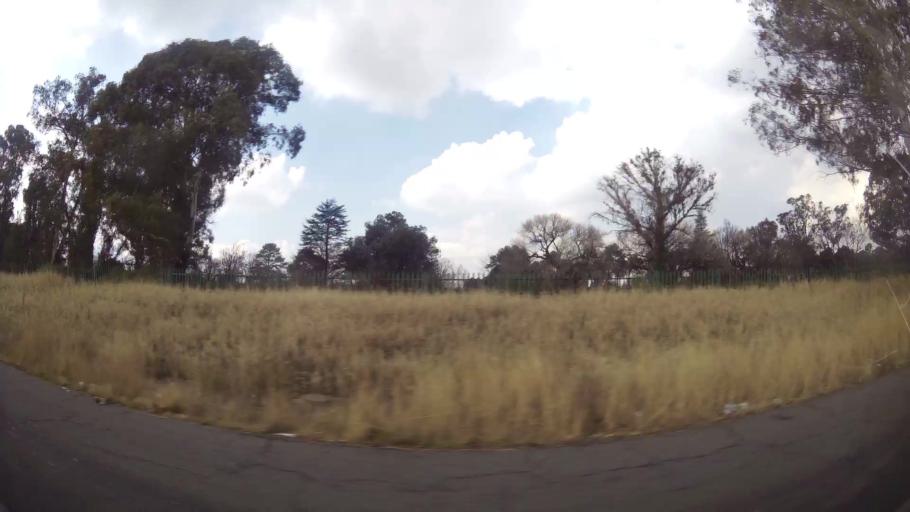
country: ZA
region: Gauteng
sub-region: Sedibeng District Municipality
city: Vereeniging
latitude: -26.6865
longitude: 27.9403
